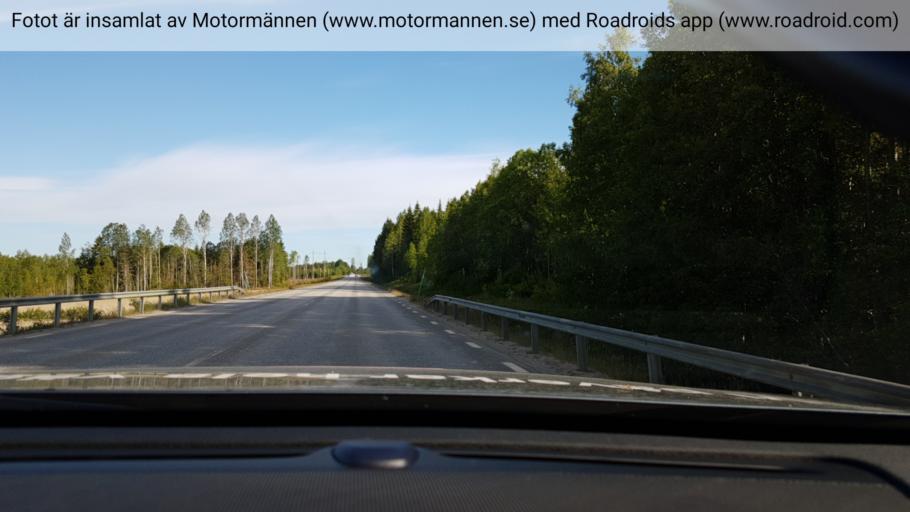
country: SE
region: Vaesterbotten
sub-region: Vannas Kommun
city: Vaennaes
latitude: 63.9703
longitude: 19.7389
